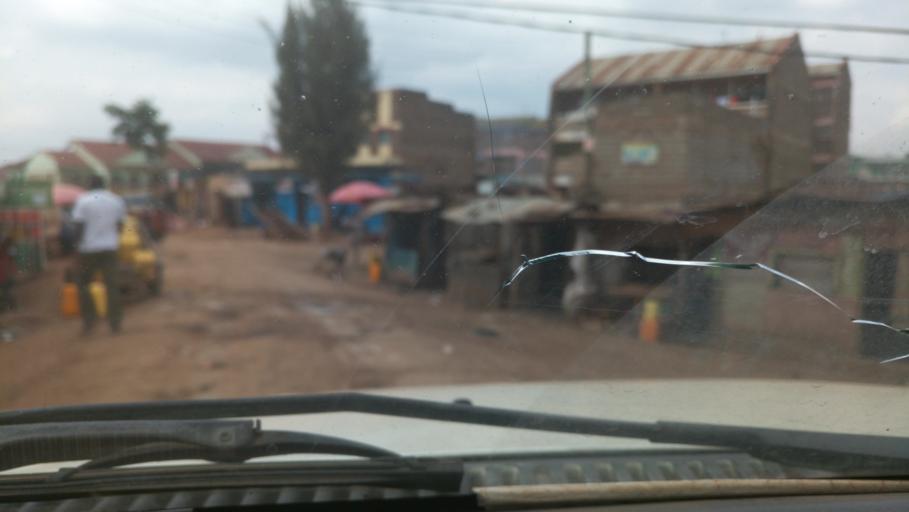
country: KE
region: Nairobi Area
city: Nairobi
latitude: -1.2957
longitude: 36.7443
